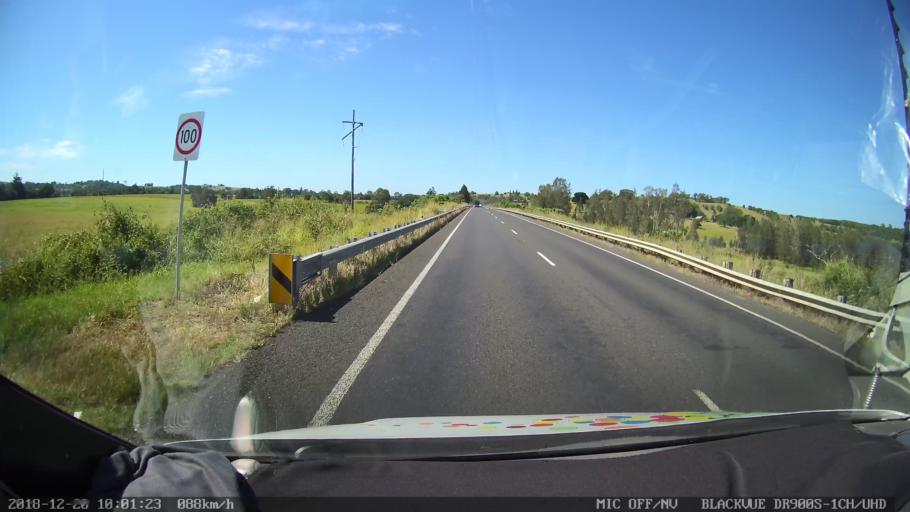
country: AU
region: New South Wales
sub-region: Lismore Municipality
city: Lismore
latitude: -28.8437
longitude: 153.2626
